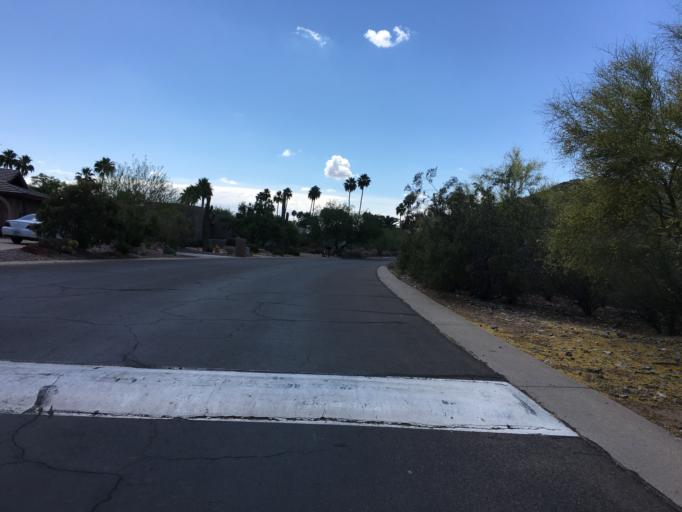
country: US
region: Arizona
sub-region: Maricopa County
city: Paradise Valley
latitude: 33.5782
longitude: -111.9885
